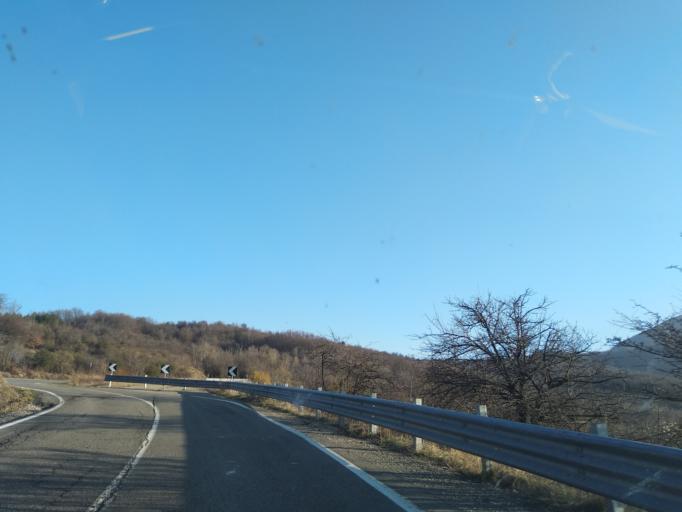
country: IT
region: Emilia-Romagna
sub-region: Provincia di Reggio Emilia
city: Busana
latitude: 44.4088
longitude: 10.3249
